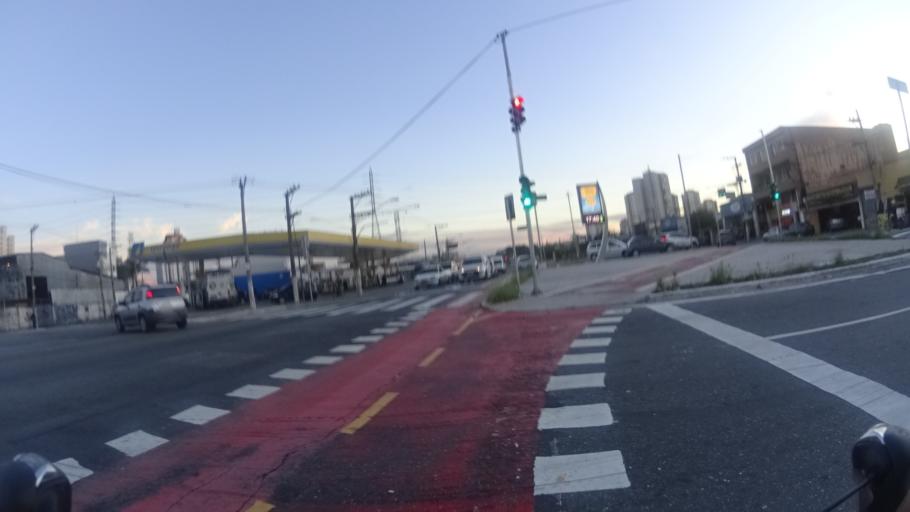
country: BR
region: Sao Paulo
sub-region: Sao Paulo
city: Sao Paulo
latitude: -23.5035
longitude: -46.6673
